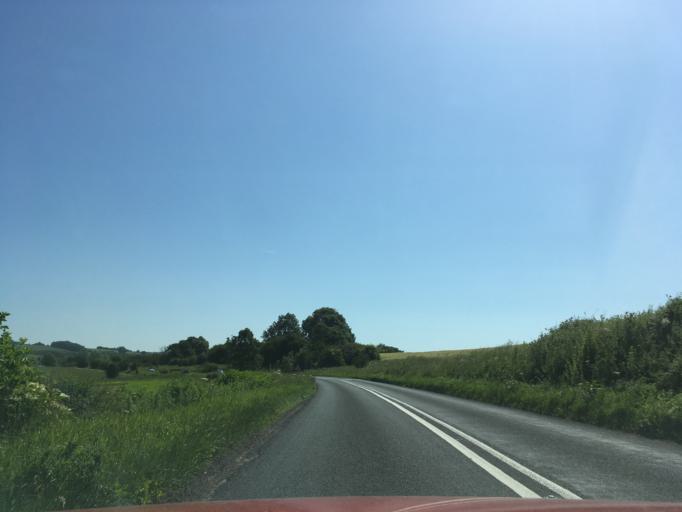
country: GB
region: England
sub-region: Gloucestershire
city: Shipton Village
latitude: 51.8768
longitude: -1.9547
